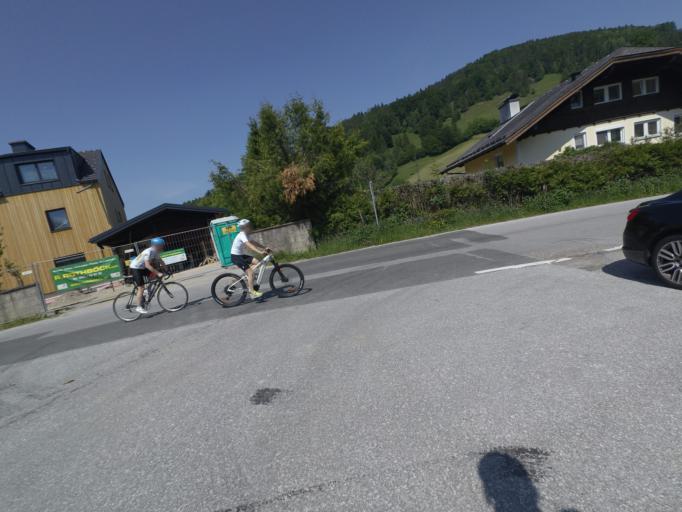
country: AT
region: Salzburg
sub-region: Politischer Bezirk Salzburg-Umgebung
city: Elsbethen
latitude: 47.7764
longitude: 13.1213
